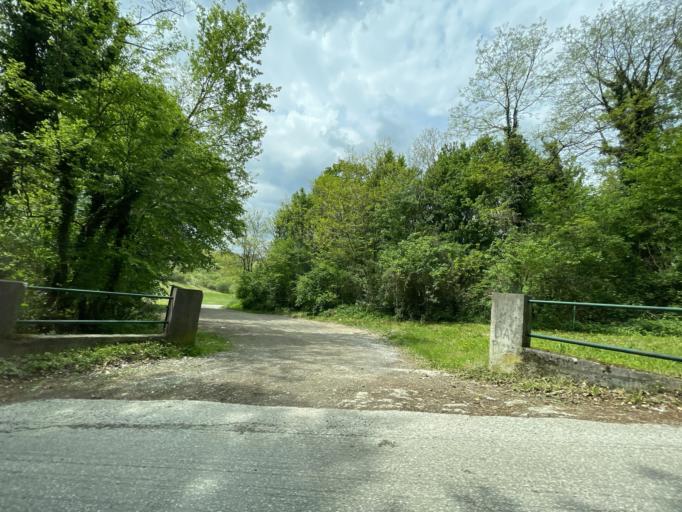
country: HR
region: Grad Zagreb
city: Zagreb
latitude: 45.8396
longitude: 15.9447
